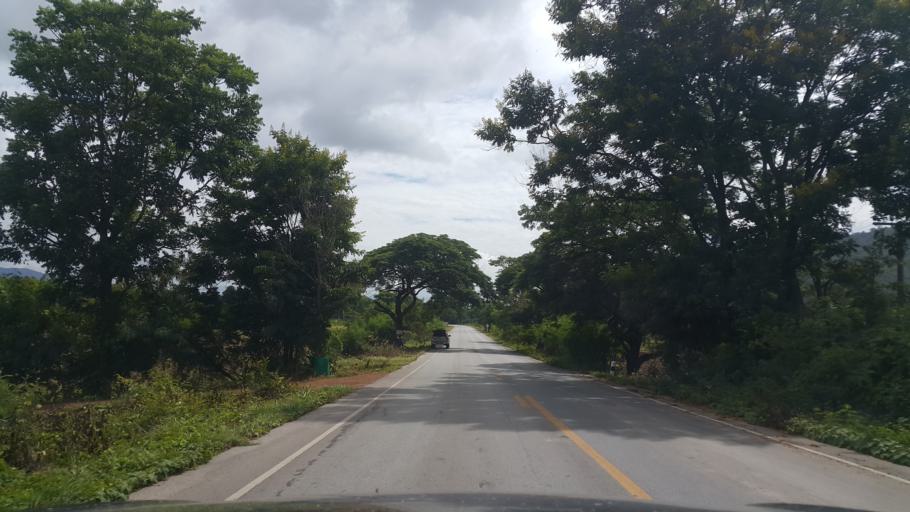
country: TH
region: Uttaradit
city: Thong Saen Khan
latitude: 17.4021
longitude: 100.3164
